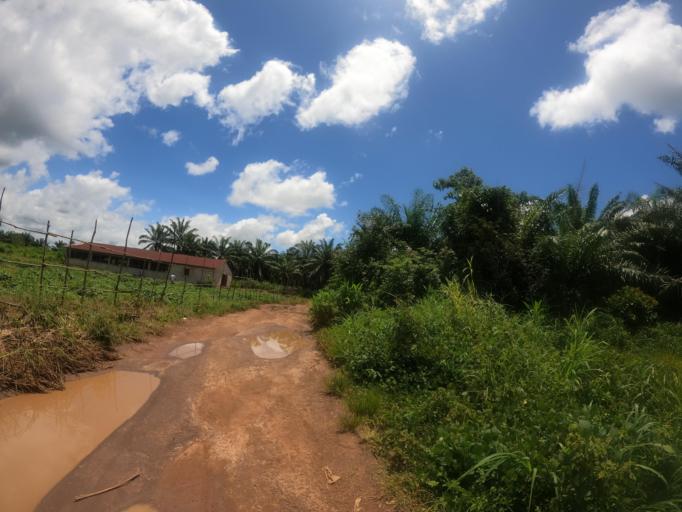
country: SL
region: Northern Province
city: Makeni
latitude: 8.8691
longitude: -12.1046
